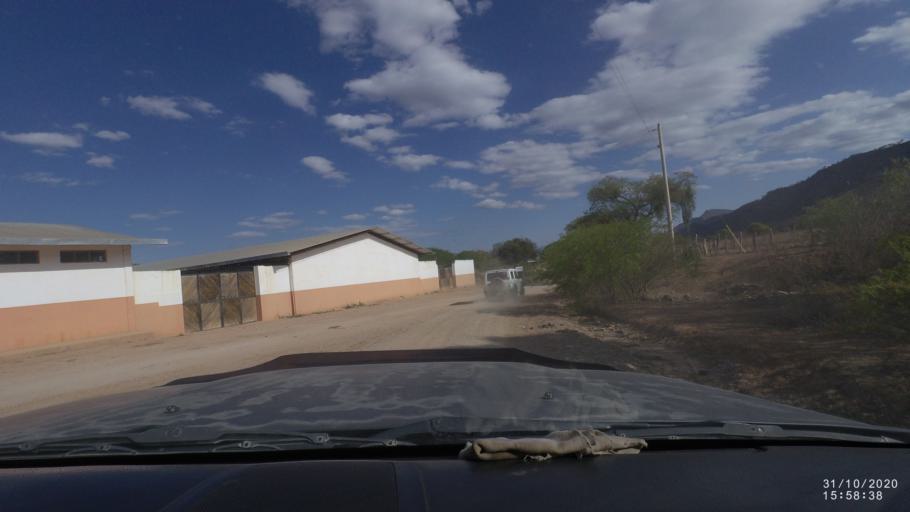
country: BO
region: Chuquisaca
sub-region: Provincia Zudanez
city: Mojocoya
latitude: -18.3261
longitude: -64.6711
